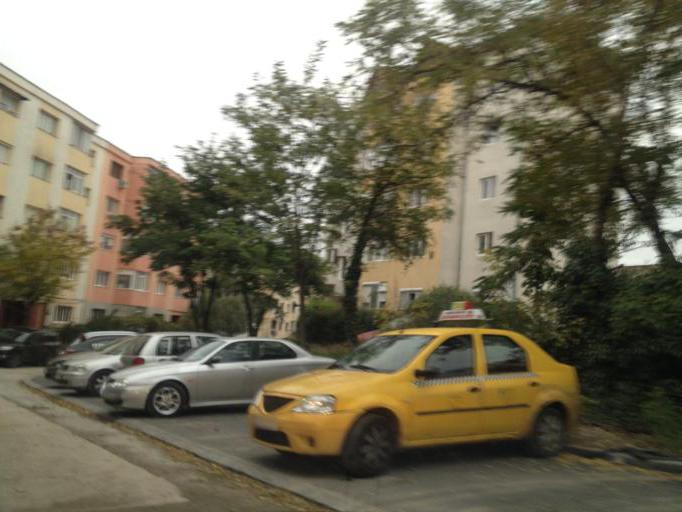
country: RO
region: Dolj
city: Craiova
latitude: 44.3323
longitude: 23.7912
